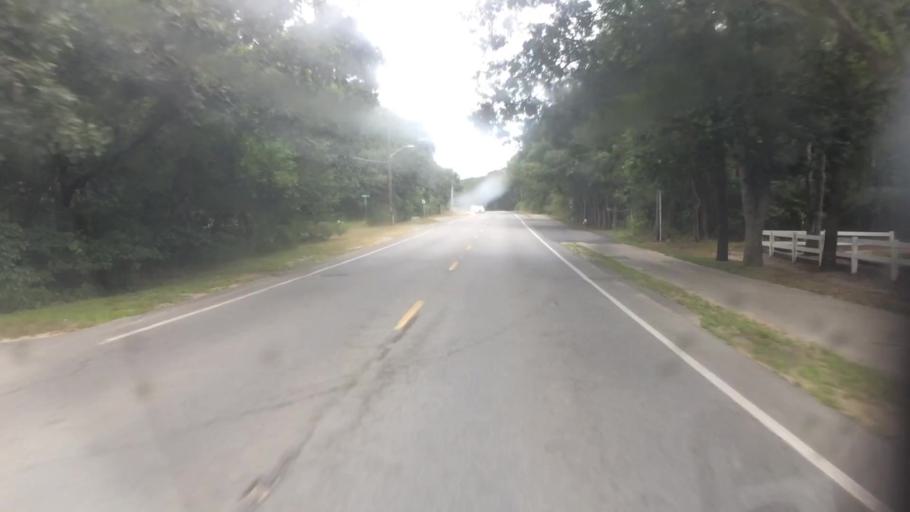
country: US
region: Massachusetts
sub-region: Dukes County
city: Edgartown
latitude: 41.4027
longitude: -70.5549
